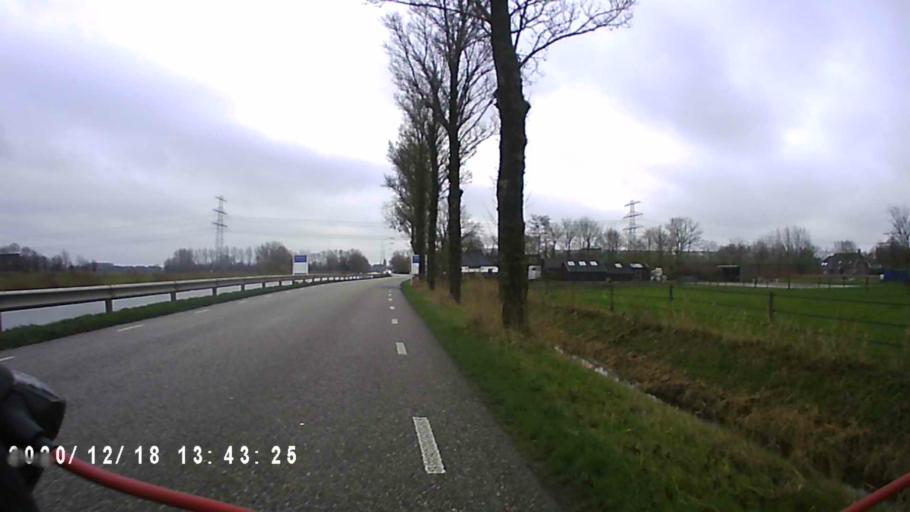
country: NL
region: Groningen
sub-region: Gemeente Bedum
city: Bedum
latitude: 53.3155
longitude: 6.5979
